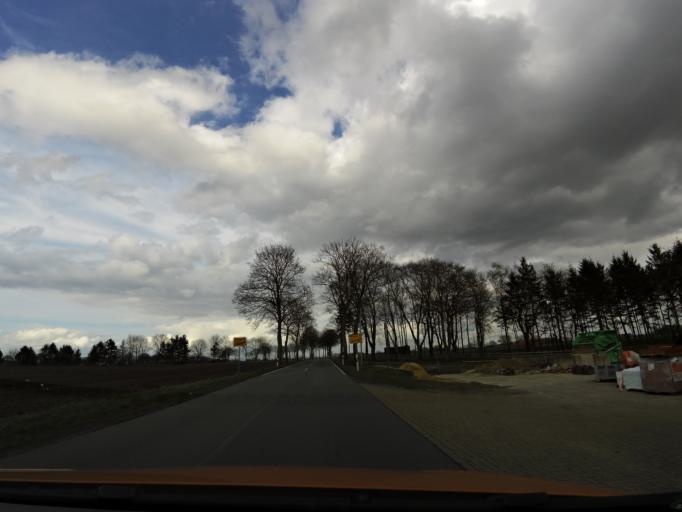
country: DE
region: Lower Saxony
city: Bassum
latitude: 52.8938
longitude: 8.7192
